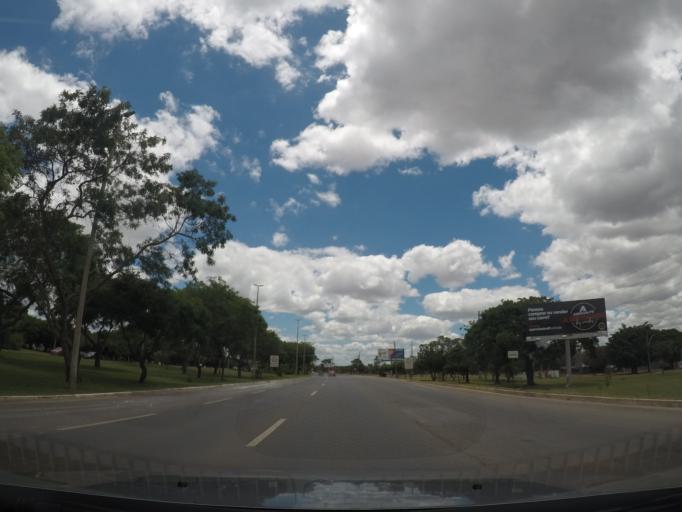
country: BR
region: Federal District
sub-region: Brasilia
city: Brasilia
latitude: -15.7694
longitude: -47.9354
